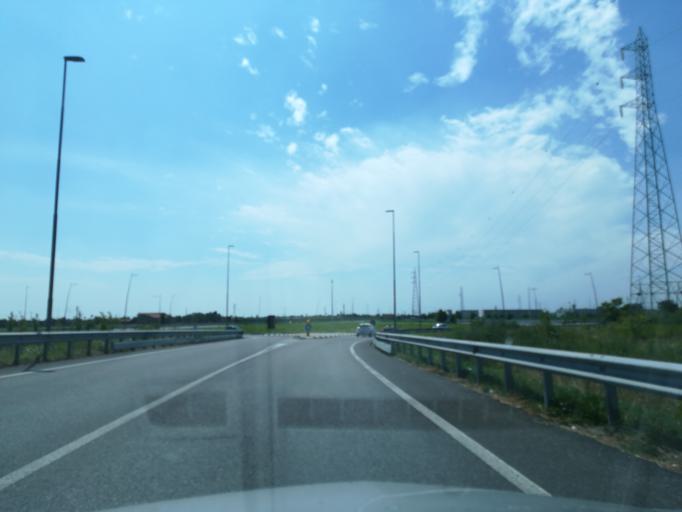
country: IT
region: Lombardy
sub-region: Provincia di Bergamo
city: Zanica
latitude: 45.6282
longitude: 9.6898
